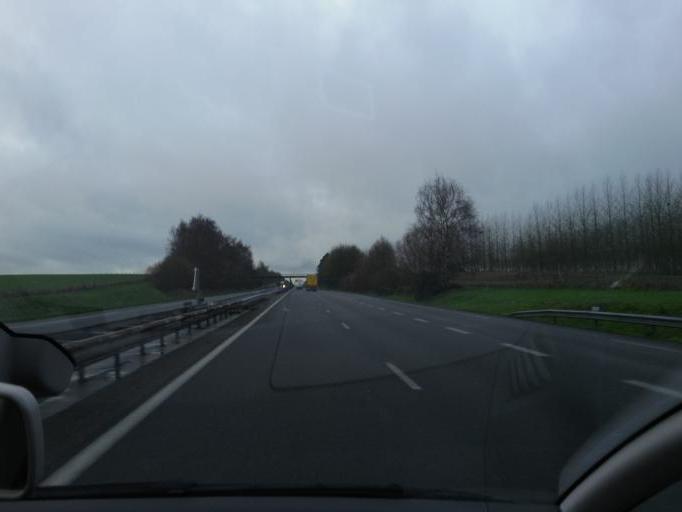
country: FR
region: Picardie
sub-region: Departement de la Somme
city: Moislains
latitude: 50.0532
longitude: 2.9425
